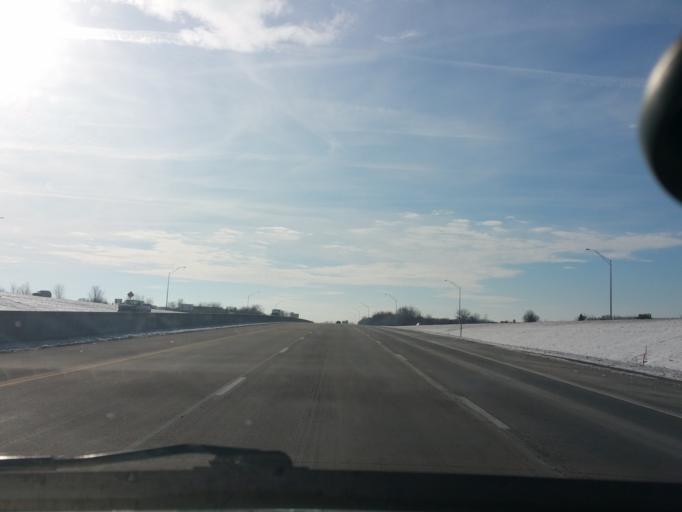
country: US
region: Iowa
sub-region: Polk County
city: West Des Moines
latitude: 41.5590
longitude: -93.7768
